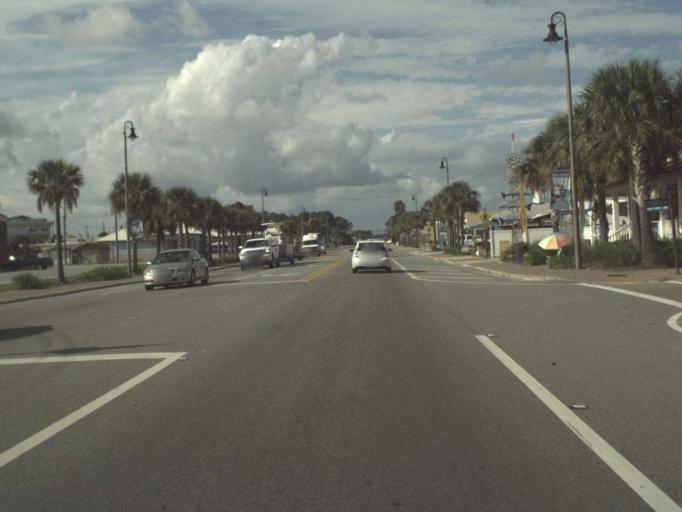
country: US
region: Florida
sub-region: Gulf County
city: Port Saint Joe
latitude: 29.8126
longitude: -85.3036
